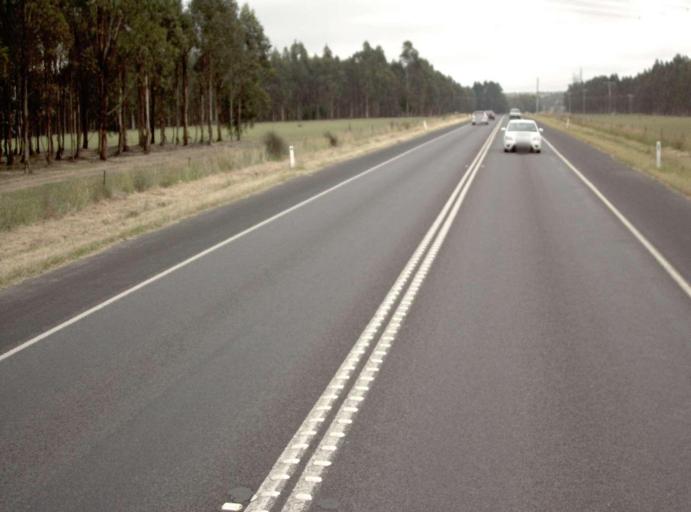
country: AU
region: Victoria
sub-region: Latrobe
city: Morwell
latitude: -38.2888
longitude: 146.4142
